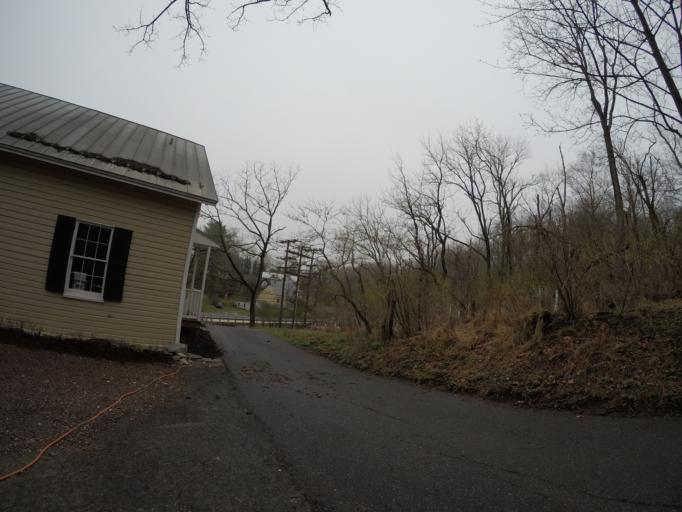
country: US
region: Maryland
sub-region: Howard County
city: Ellicott City
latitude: 39.2688
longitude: -76.8108
